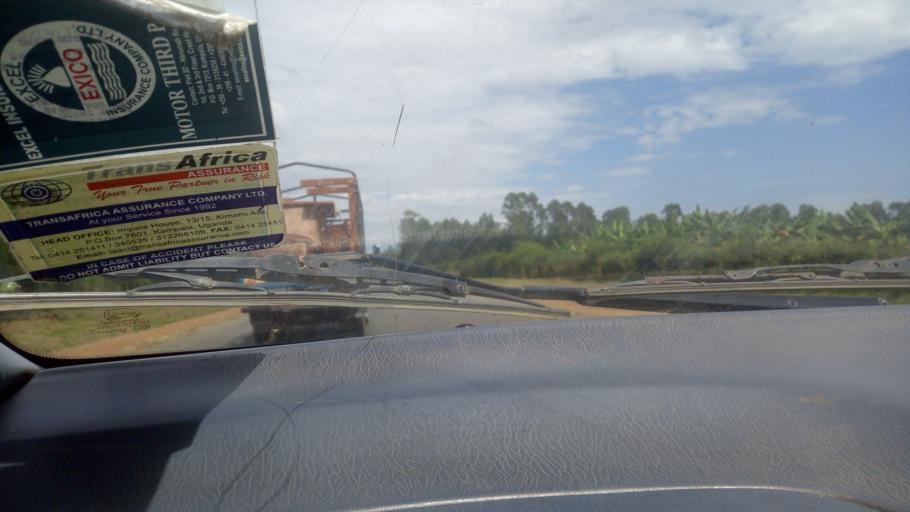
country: UG
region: Western Region
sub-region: Mbarara District
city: Bwizibwera
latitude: -0.4254
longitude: 30.5709
